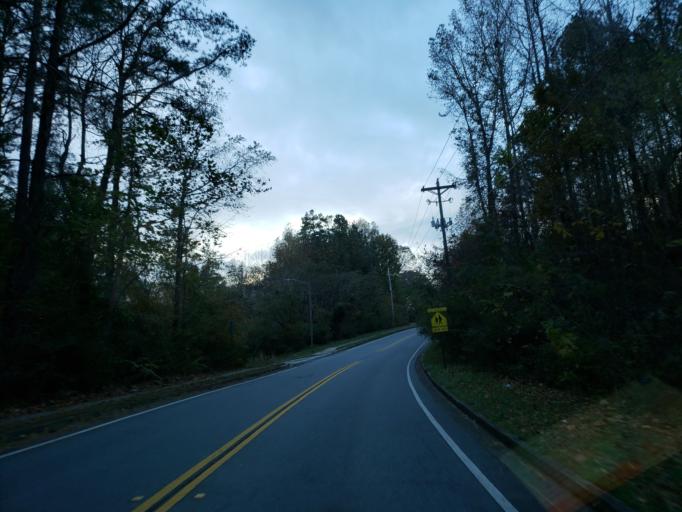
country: US
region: Georgia
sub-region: Cobb County
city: Acworth
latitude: 34.0154
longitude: -84.6686
